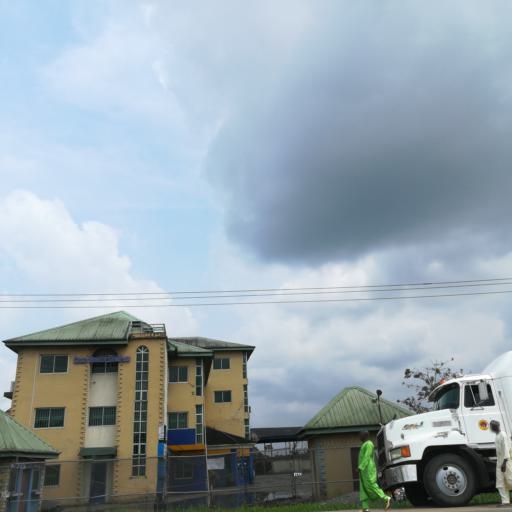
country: NG
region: Rivers
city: Port Harcourt
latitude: 4.8511
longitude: 7.0716
